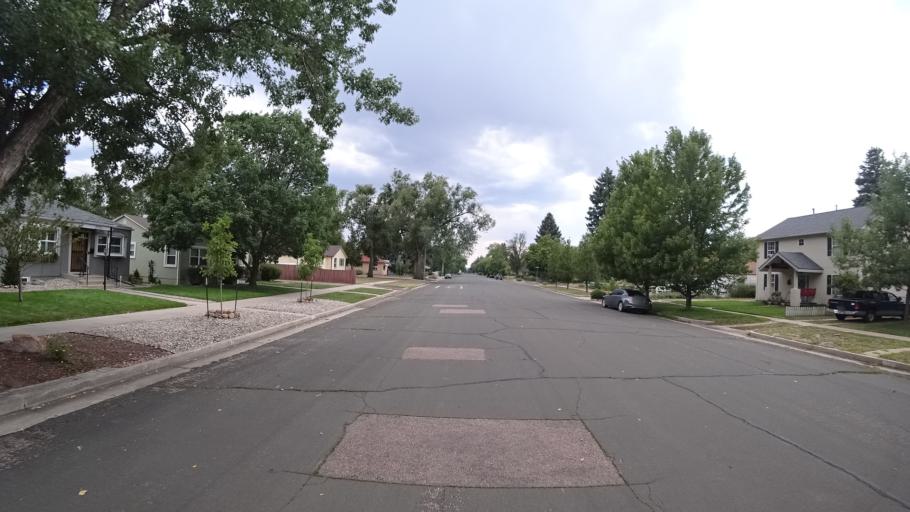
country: US
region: Colorado
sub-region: El Paso County
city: Colorado Springs
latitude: 38.8635
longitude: -104.8147
